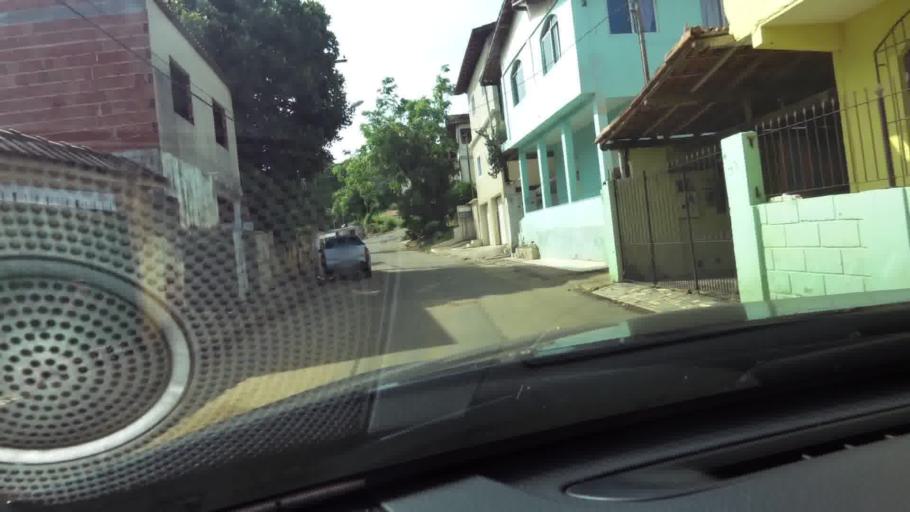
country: BR
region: Espirito Santo
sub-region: Guarapari
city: Guarapari
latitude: -20.6263
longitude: -40.4699
